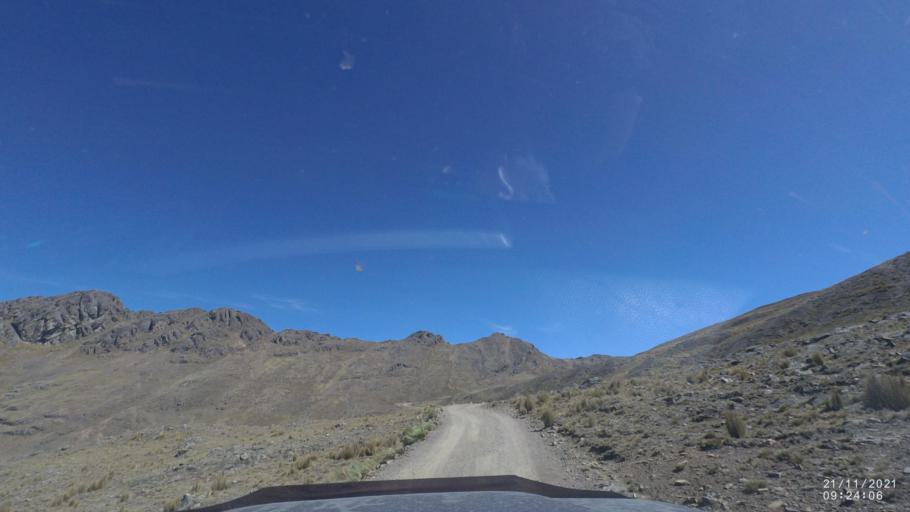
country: BO
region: Cochabamba
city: Cochabamba
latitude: -17.0938
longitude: -66.2547
